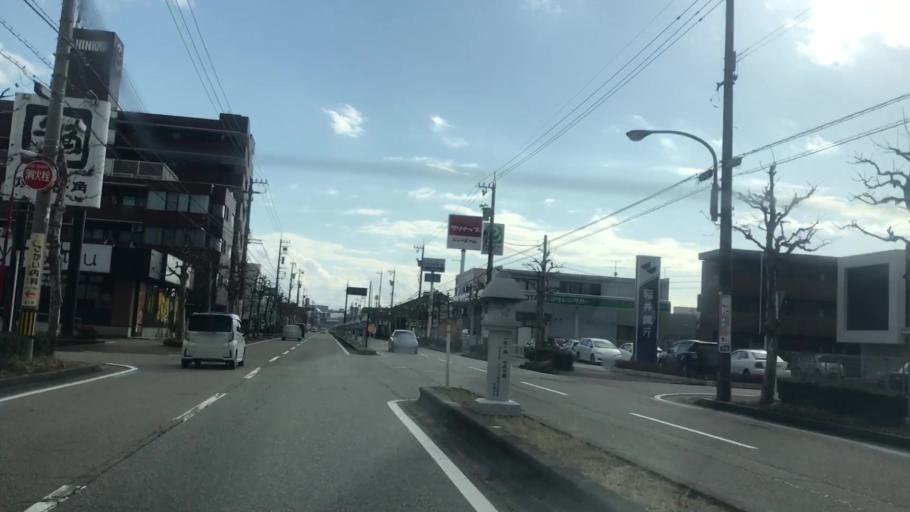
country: JP
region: Toyama
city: Takaoka
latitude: 36.7341
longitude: 137.0155
